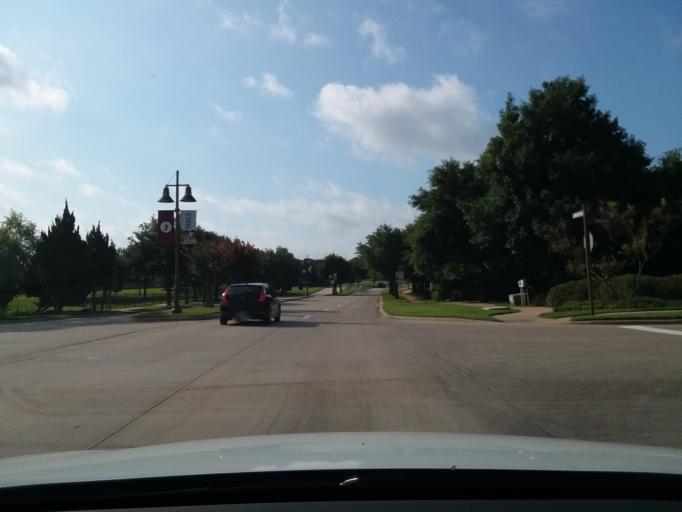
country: US
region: Texas
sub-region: Denton County
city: Bartonville
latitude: 33.0776
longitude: -97.1249
